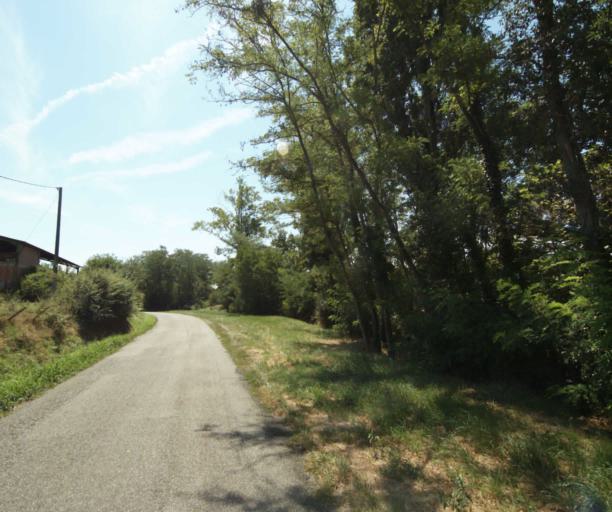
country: FR
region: Midi-Pyrenees
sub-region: Departement de l'Ariege
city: Lezat-sur-Leze
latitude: 43.2720
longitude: 1.3382
